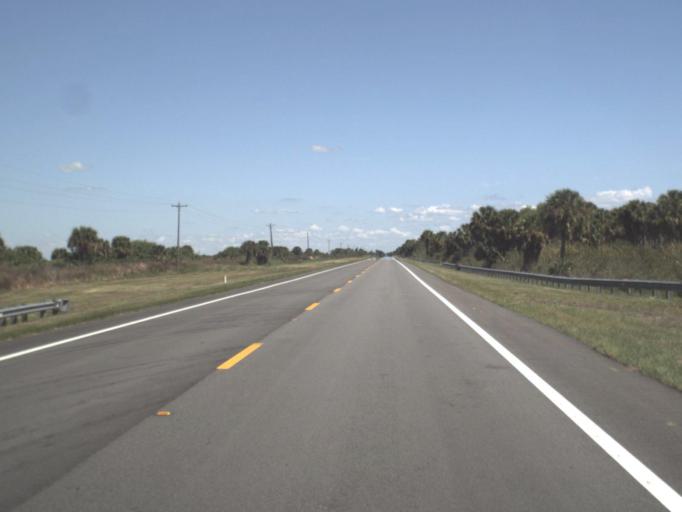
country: US
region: Florida
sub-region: Glades County
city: Buckhead Ridge
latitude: 27.0217
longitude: -81.0183
